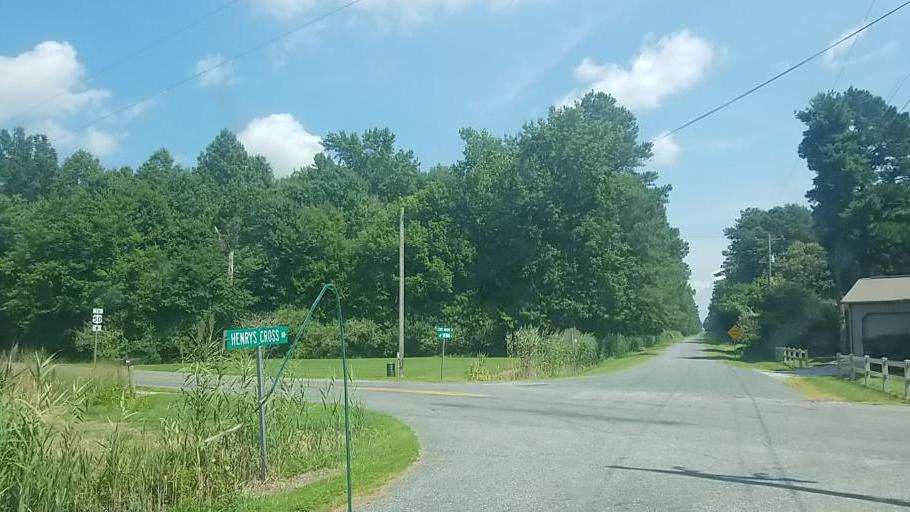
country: US
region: Maryland
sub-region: Wicomico County
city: Hebron
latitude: 38.4216
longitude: -75.8684
